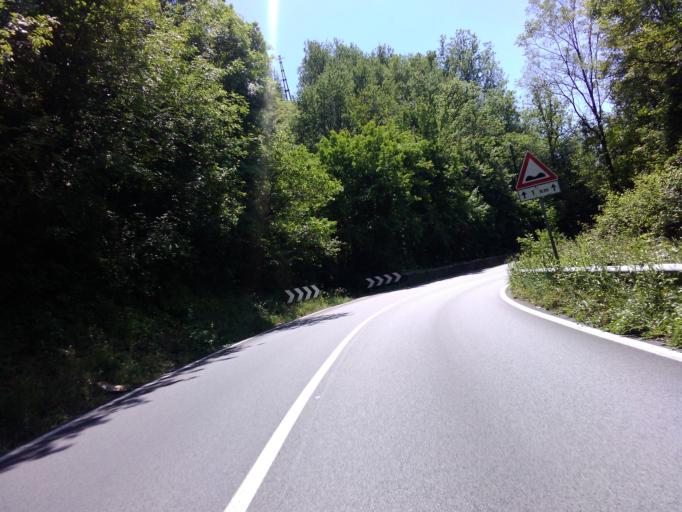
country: IT
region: Tuscany
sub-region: Provincia di Massa-Carrara
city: Villafranca in Lunigiana
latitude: 44.2721
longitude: 9.9547
